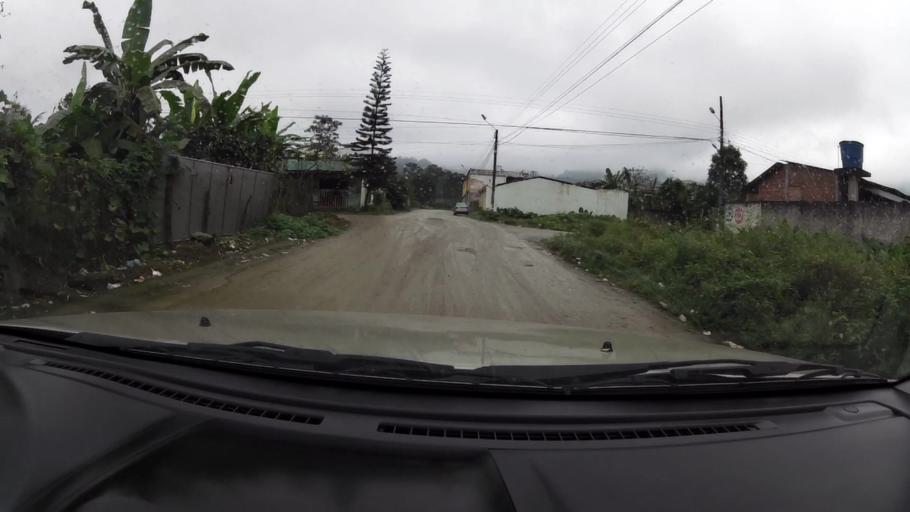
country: EC
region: Guayas
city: Balao
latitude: -3.0611
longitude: -79.7444
